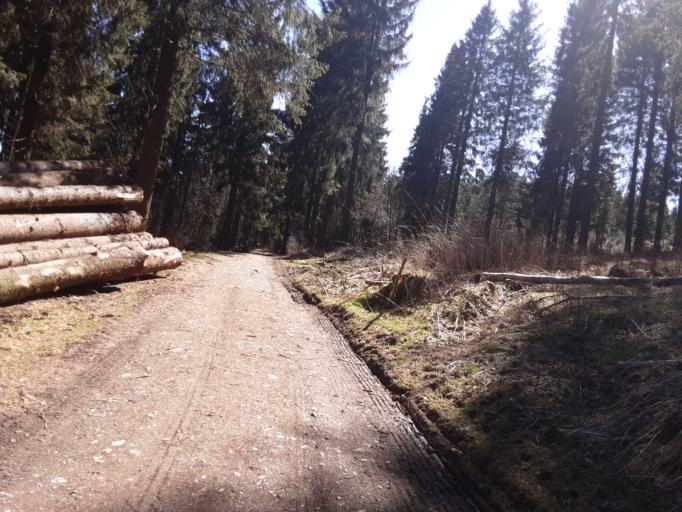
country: DE
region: North Rhine-Westphalia
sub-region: Regierungsbezirk Arnsberg
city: Winterberg
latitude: 51.1915
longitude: 8.4698
